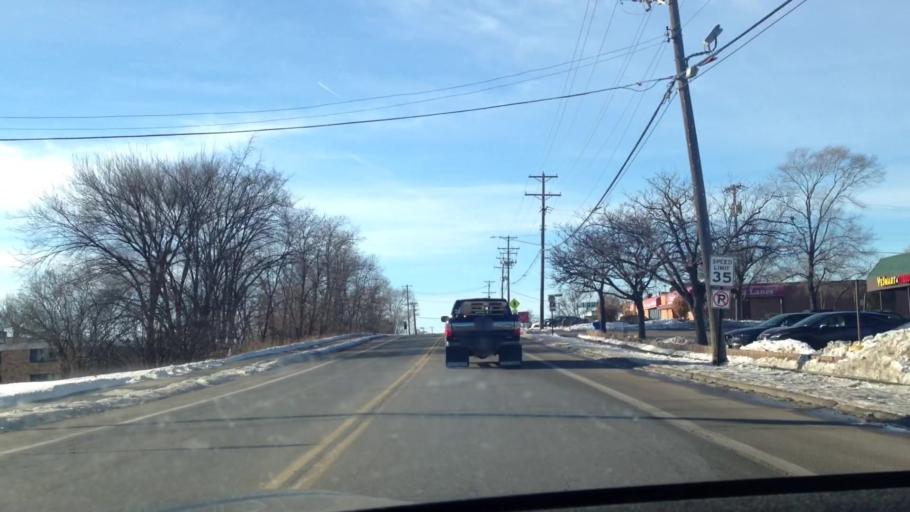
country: US
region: Minnesota
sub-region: Hennepin County
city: Saint Louis Park
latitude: 44.9495
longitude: -93.3825
